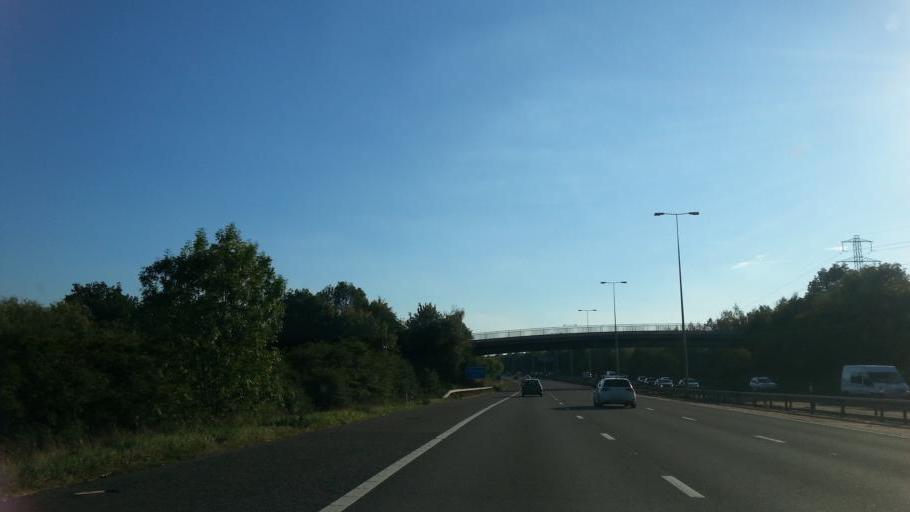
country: GB
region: England
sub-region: Worcestershire
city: Fernhill Heath
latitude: 52.2011
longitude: -2.1636
